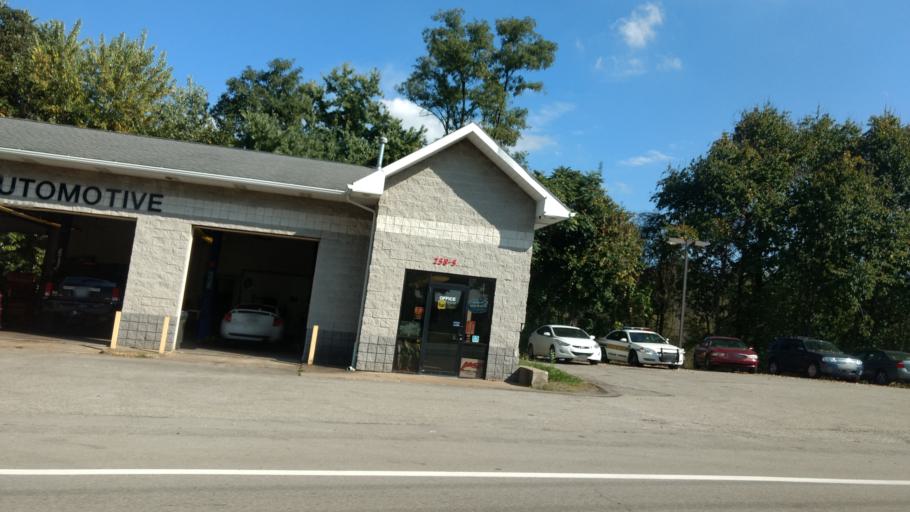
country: US
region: Pennsylvania
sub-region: Washington County
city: Wickerham Manor-Fisher
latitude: 40.1830
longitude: -79.9165
